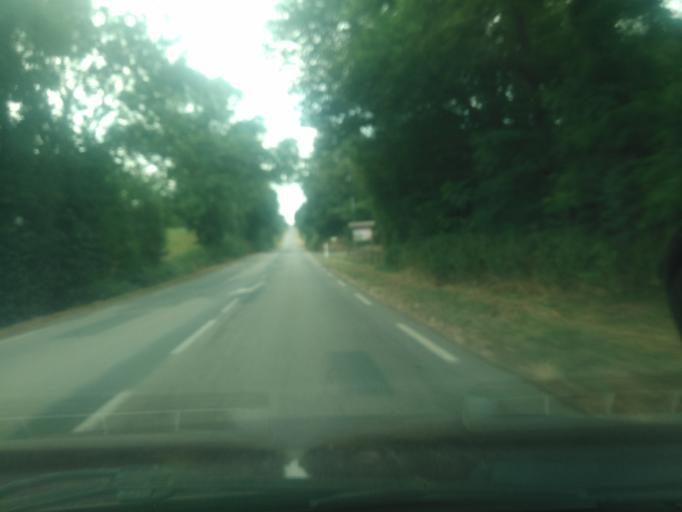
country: FR
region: Poitou-Charentes
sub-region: Departement des Deux-Sevres
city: Secondigny
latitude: 46.6222
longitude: -0.4700
